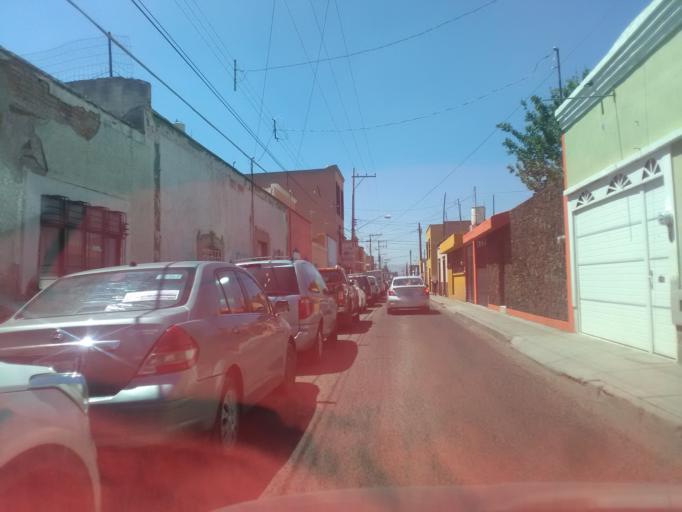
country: MX
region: Durango
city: Victoria de Durango
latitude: 24.0232
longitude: -104.6605
